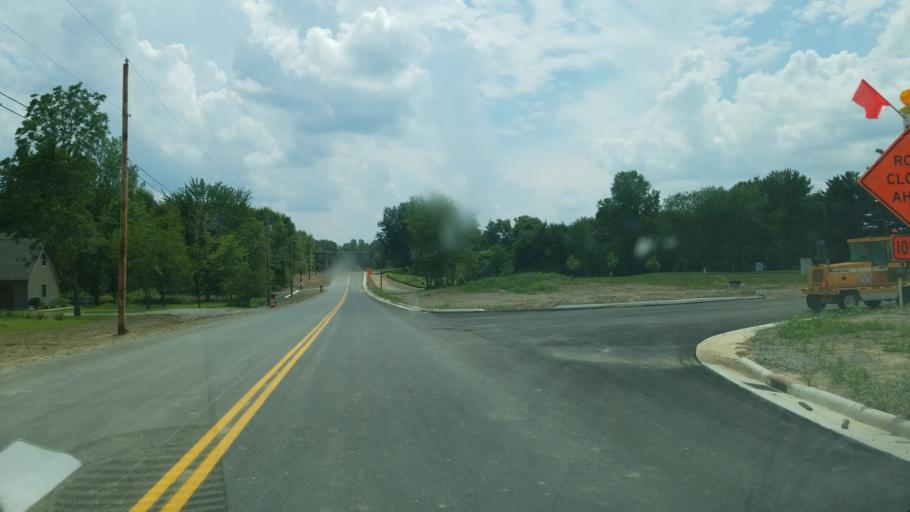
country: US
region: Ohio
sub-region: Delaware County
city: Lewis Center
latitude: 40.2034
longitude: -83.0139
